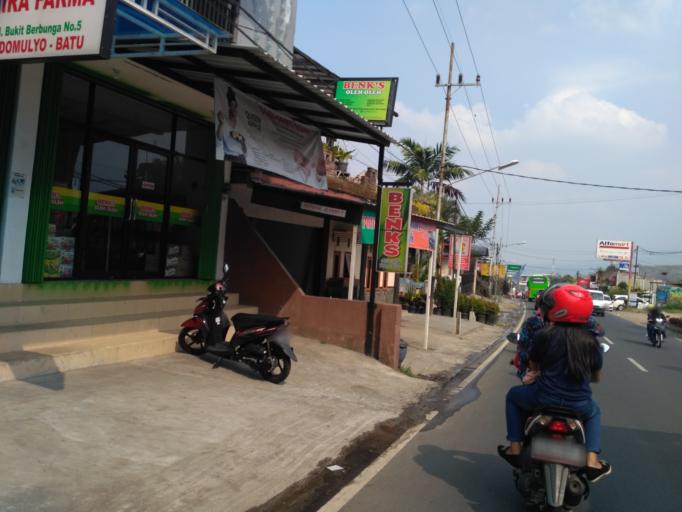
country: ID
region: East Java
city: Batu
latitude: -7.8454
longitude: 112.5283
